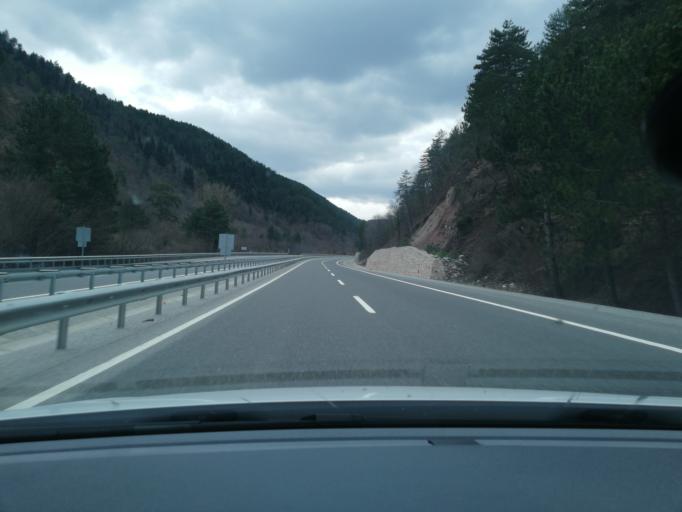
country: TR
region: Bolu
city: Yenicaga
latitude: 40.8510
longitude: 32.0685
